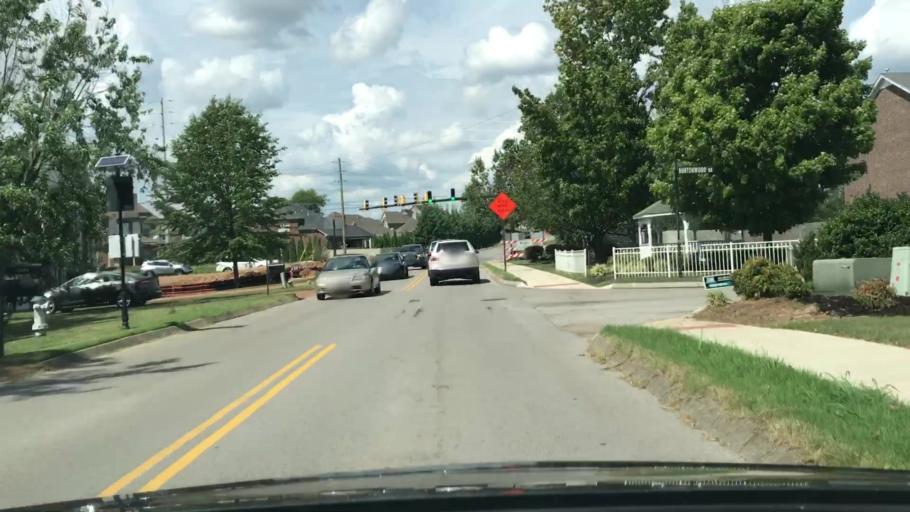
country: US
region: Tennessee
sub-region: Maury County
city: Spring Hill
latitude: 35.7520
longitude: -86.8838
